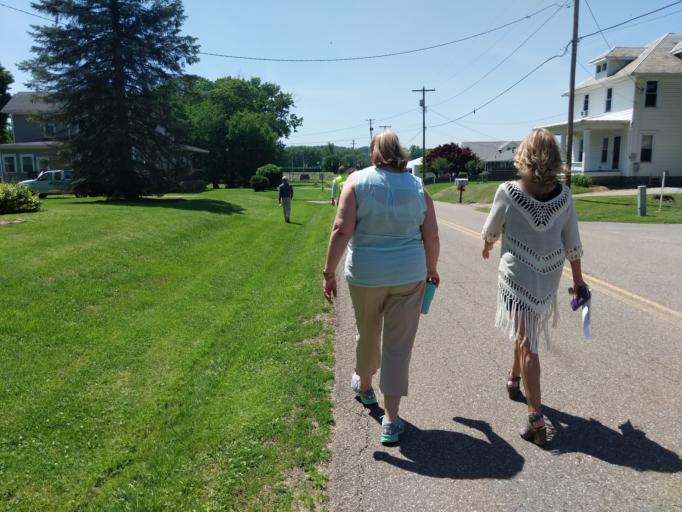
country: US
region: Ohio
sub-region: Washington County
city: Reno
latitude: 39.3920
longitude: -81.4023
